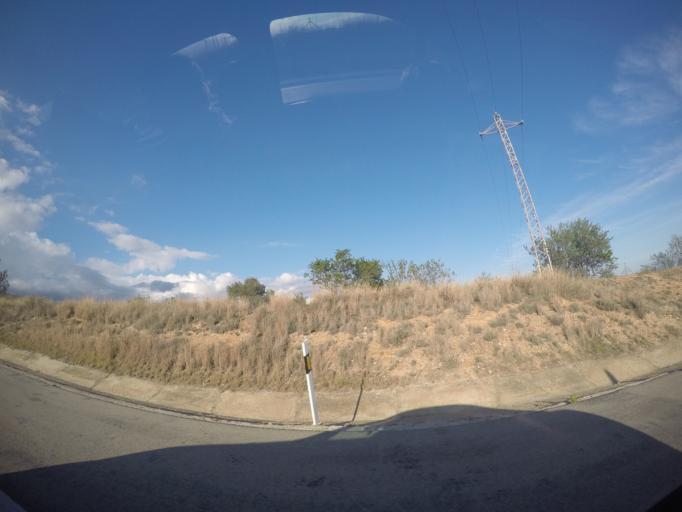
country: ES
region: Catalonia
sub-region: Provincia de Tarragona
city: la Bisbal del Penedes
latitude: 41.2809
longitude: 1.4978
